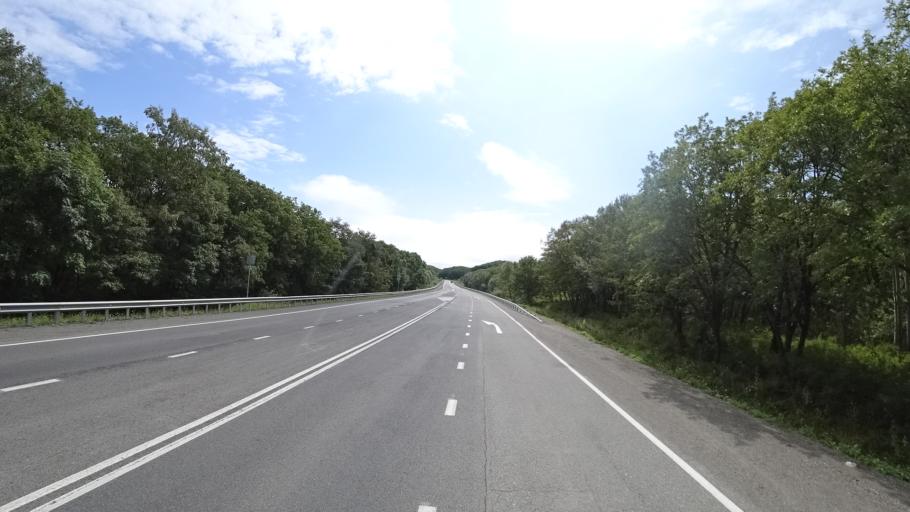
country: RU
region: Primorskiy
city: Lyalichi
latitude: 44.1381
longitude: 132.4286
